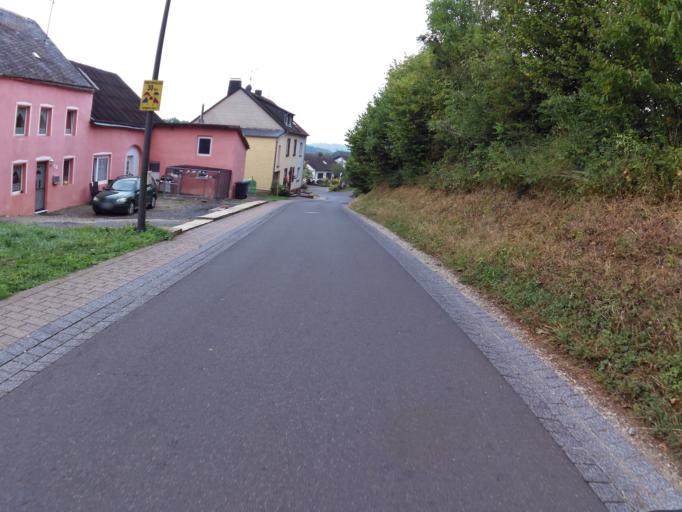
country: DE
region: Rheinland-Pfalz
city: Wilsecker
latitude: 50.0269
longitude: 6.5803
